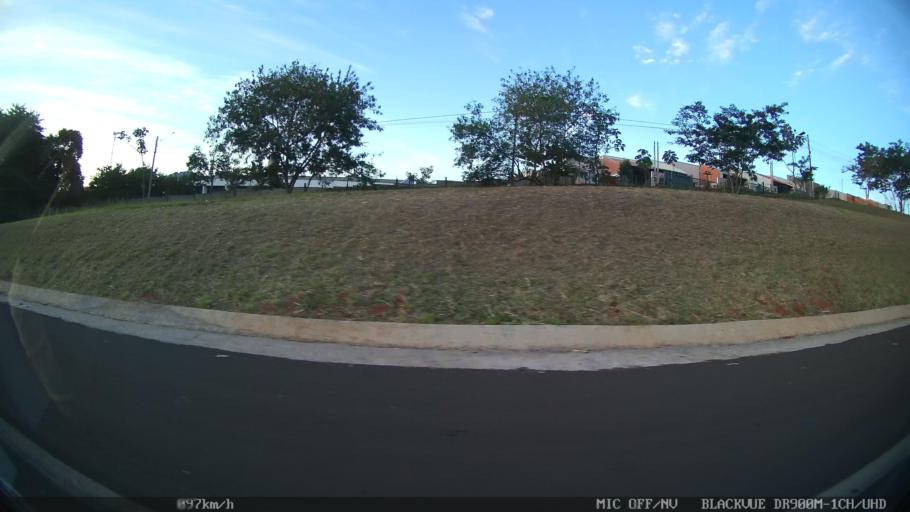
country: BR
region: Sao Paulo
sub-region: Catanduva
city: Catanduva
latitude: -21.1696
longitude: -48.9737
